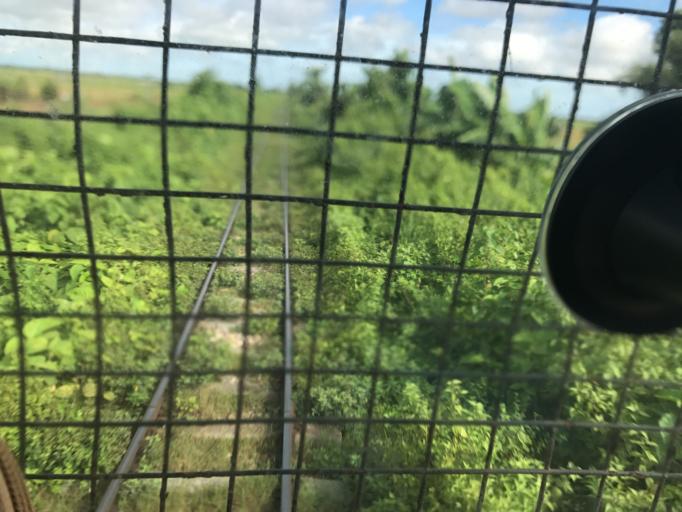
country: MM
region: Bago
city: Letpandan
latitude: 18.0011
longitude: 95.7030
